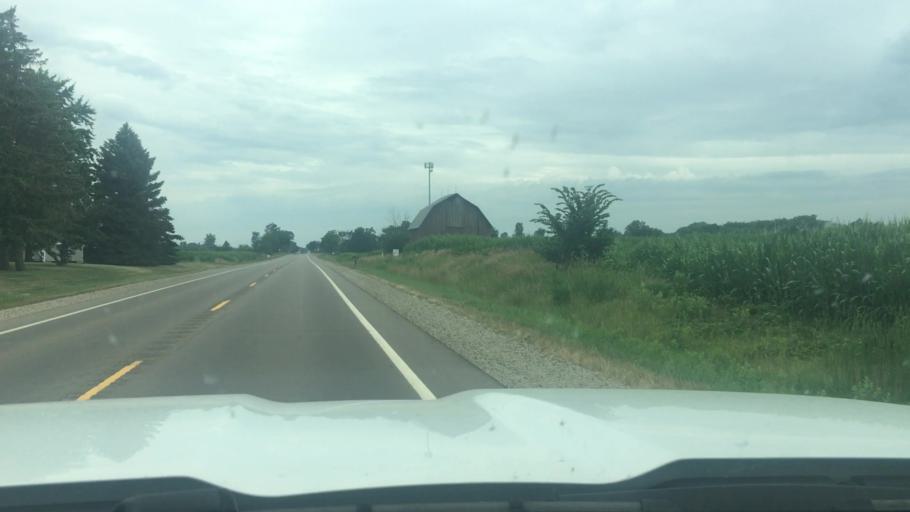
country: US
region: Michigan
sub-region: Clinton County
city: Saint Johns
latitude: 43.0016
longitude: -84.6463
